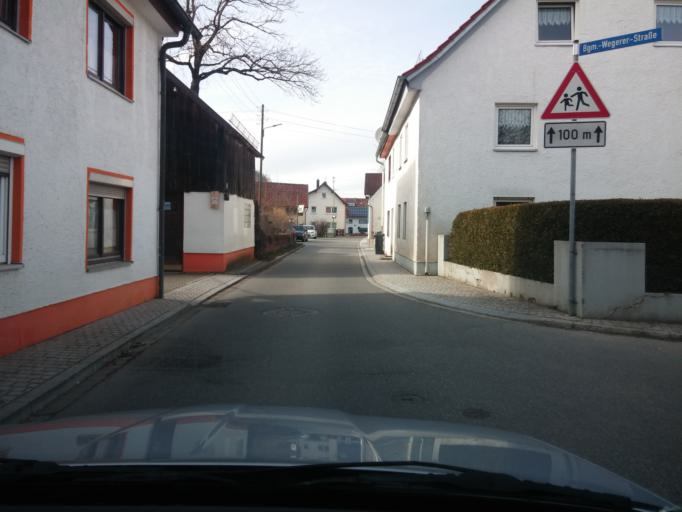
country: DE
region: Bavaria
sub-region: Swabia
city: Trunkelsberg
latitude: 48.0014
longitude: 10.2201
